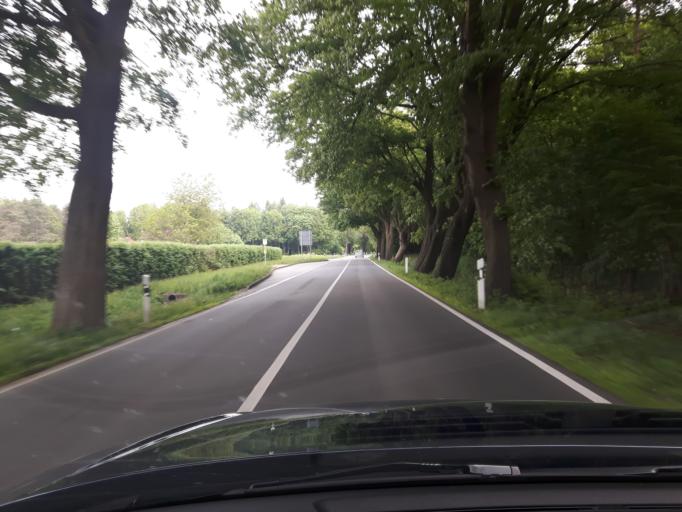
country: DE
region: Mecklenburg-Vorpommern
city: Gross Wokern
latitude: 53.6192
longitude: 12.4671
